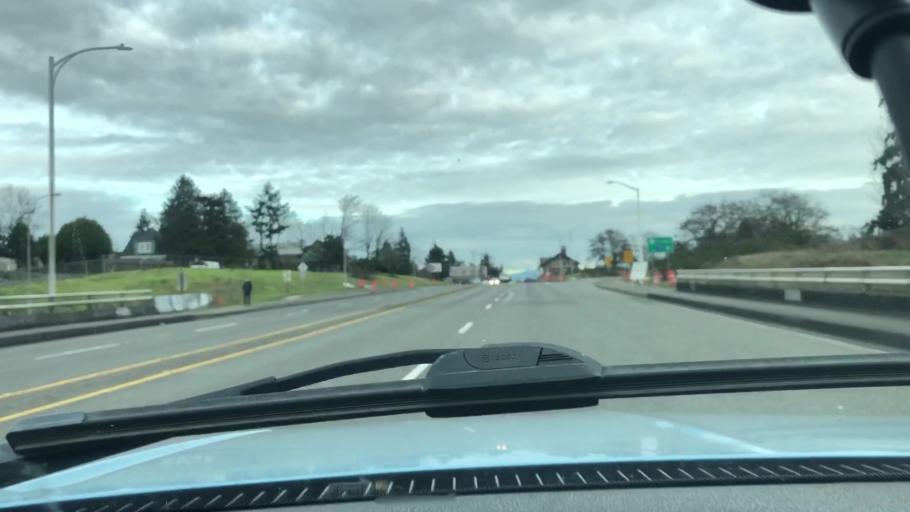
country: US
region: Washington
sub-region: Pierce County
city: Tacoma
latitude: 47.2231
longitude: -122.4255
